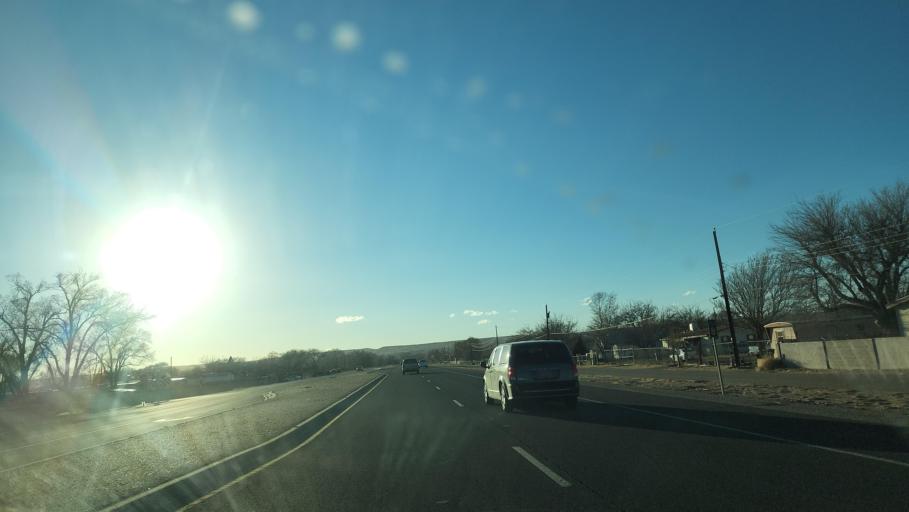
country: US
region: New Mexico
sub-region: Bernalillo County
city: South Valley
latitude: 35.0269
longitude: -106.6988
